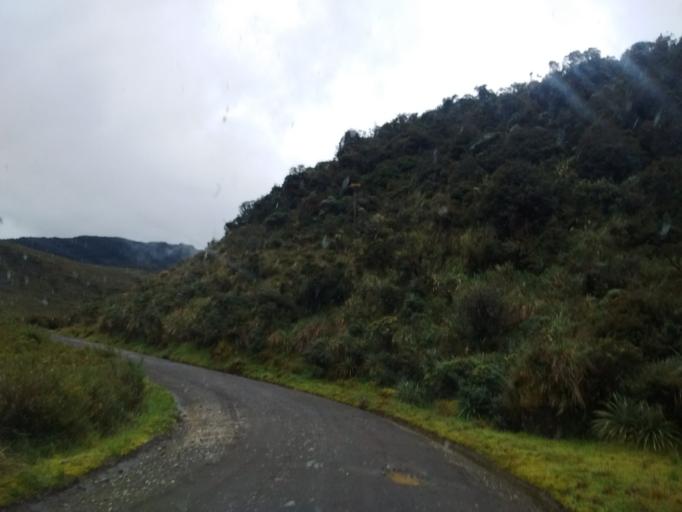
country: CO
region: Cauca
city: Totoro
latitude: 2.3575
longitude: -76.3200
